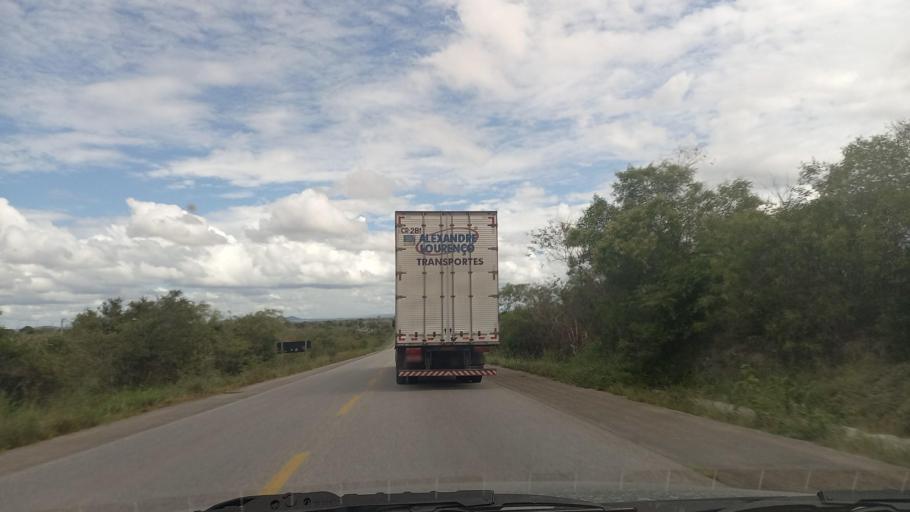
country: BR
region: Pernambuco
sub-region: Cachoeirinha
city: Cachoeirinha
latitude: -8.3852
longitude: -36.1752
